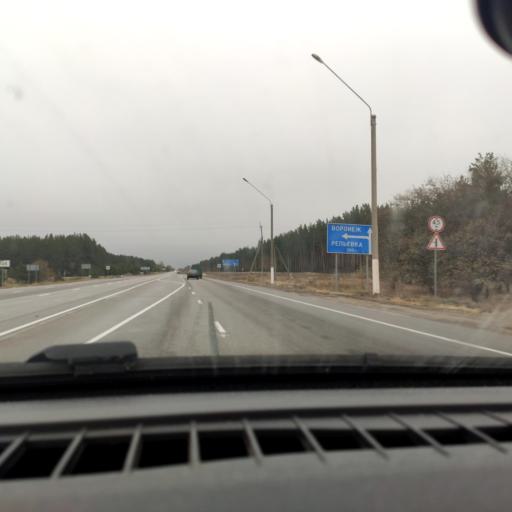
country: RU
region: Voronezj
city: Uryv-Pokrovka
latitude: 51.0474
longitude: 38.9828
